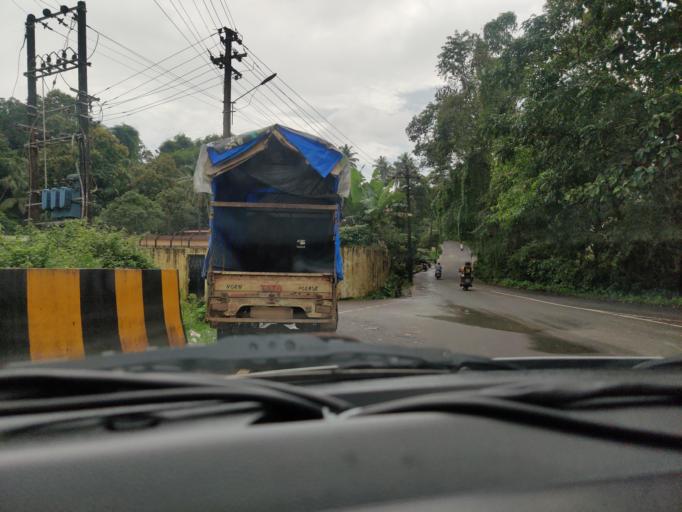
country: IN
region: Goa
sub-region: North Goa
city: Valpoy
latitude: 15.5331
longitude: 74.1407
